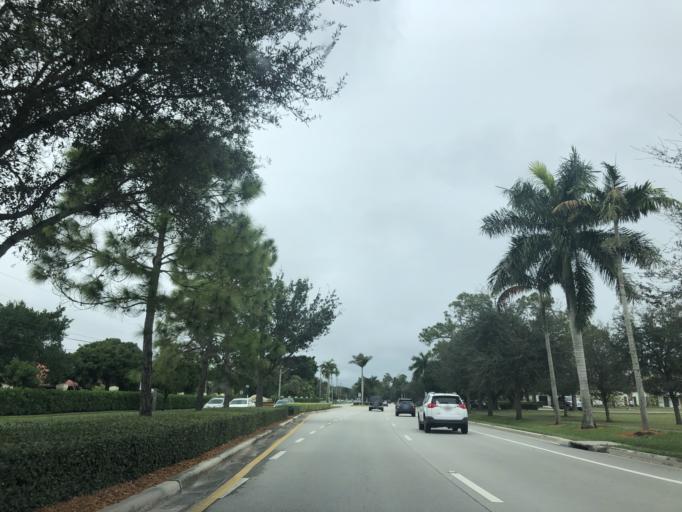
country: US
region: Florida
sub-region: Palm Beach County
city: Wellington
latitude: 26.6665
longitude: -80.2455
